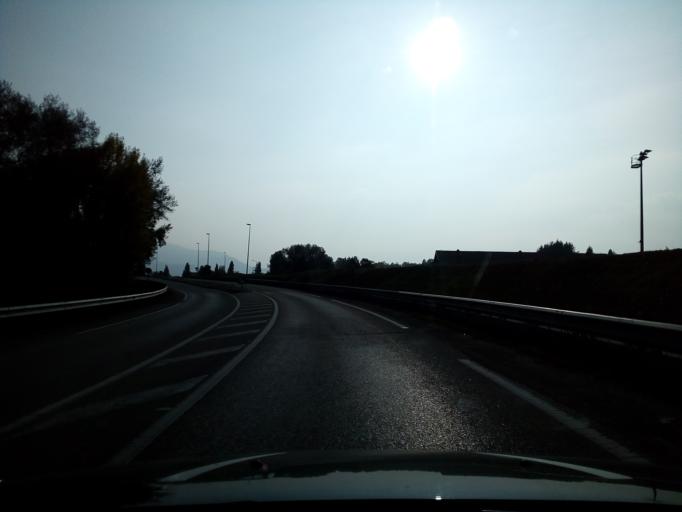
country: FR
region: Rhone-Alpes
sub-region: Departement de l'Isere
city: Montbonnot-Saint-Martin
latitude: 45.2259
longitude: 5.8206
